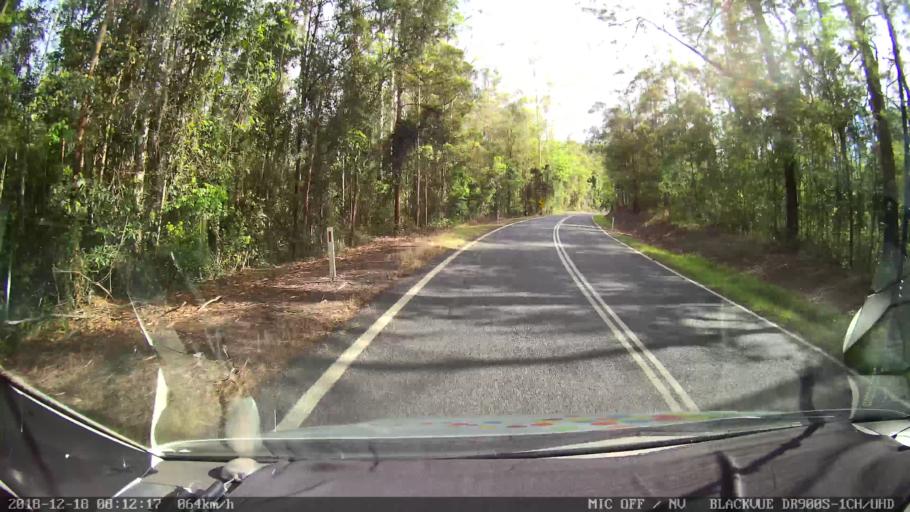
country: AU
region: New South Wales
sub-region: Kyogle
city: Kyogle
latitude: -28.3408
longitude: 152.6696
